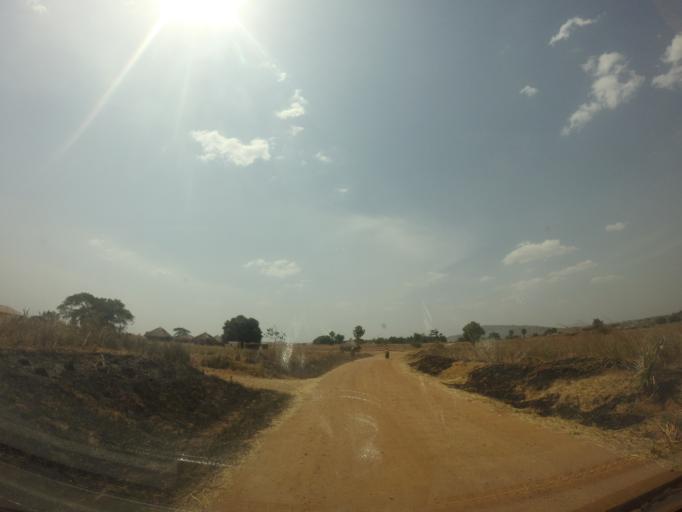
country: UG
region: Northern Region
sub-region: Arua District
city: Arua
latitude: 2.9083
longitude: 31.0551
